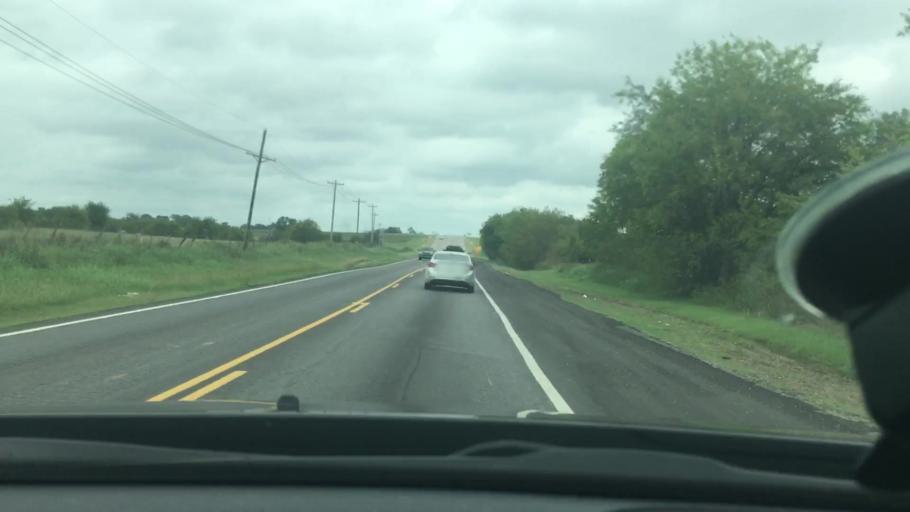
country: US
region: Oklahoma
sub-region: Bryan County
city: Durant
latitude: 33.9574
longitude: -96.3732
